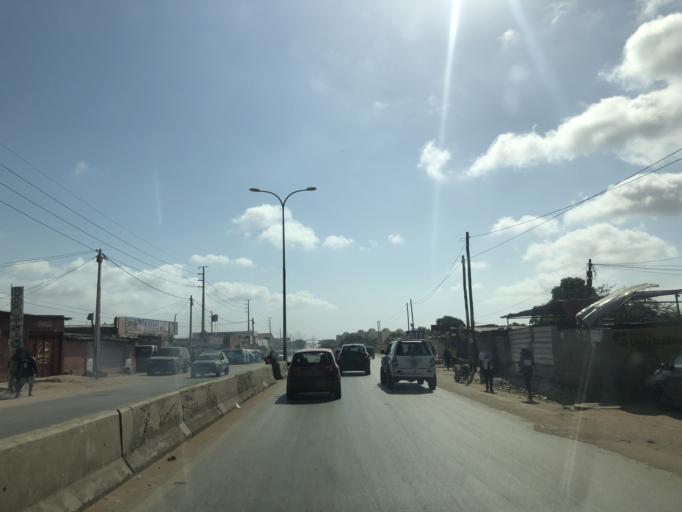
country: AO
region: Luanda
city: Luanda
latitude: -8.9041
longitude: 13.2473
